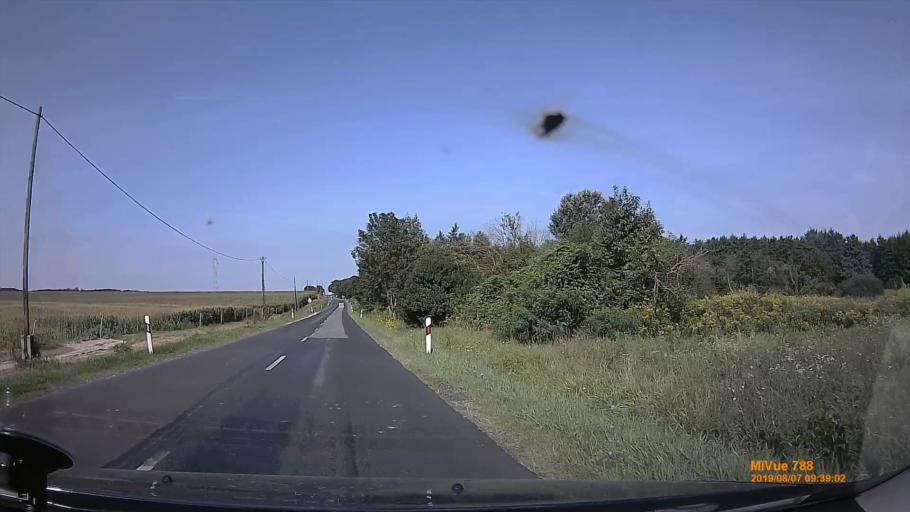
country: HU
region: Zala
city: Pacsa
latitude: 46.7301
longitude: 17.0828
